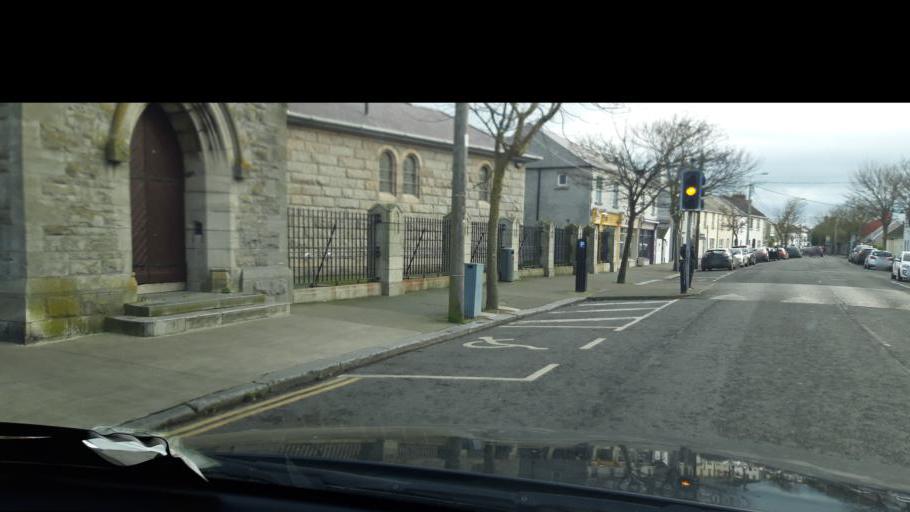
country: IE
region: Leinster
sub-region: Fingal County
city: Skerries
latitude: 53.5783
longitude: -6.1074
